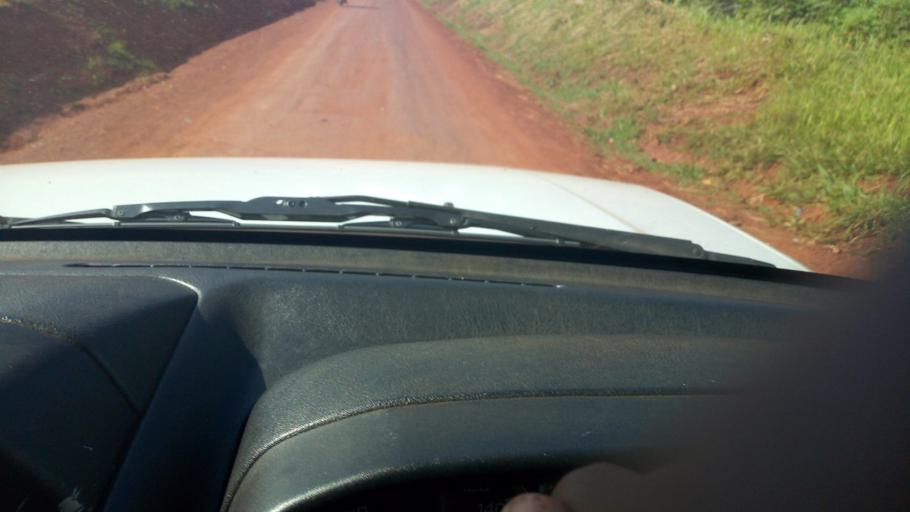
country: UG
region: Western Region
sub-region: Masindi District
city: Masindi
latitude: 1.6634
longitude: 31.7059
